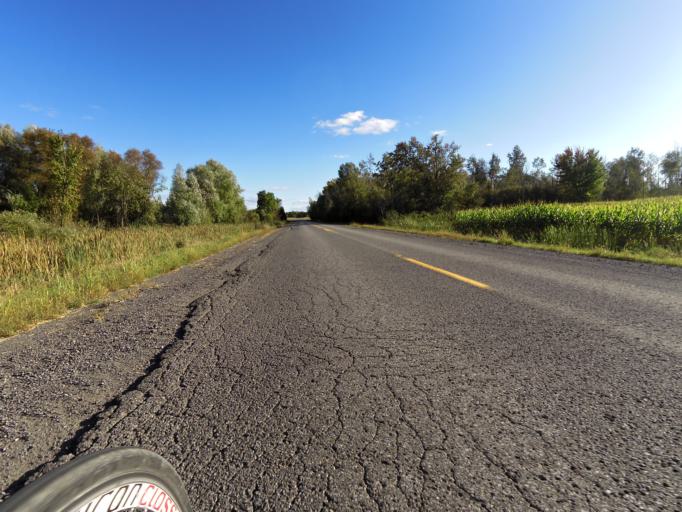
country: CA
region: Ontario
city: Bells Corners
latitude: 45.1923
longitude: -75.7857
